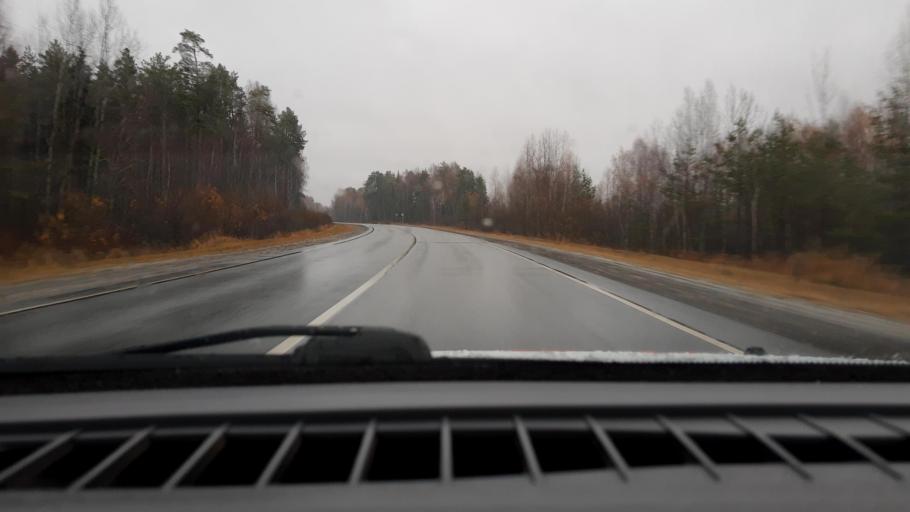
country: RU
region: Nizjnij Novgorod
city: Linda
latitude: 56.6439
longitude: 44.1123
